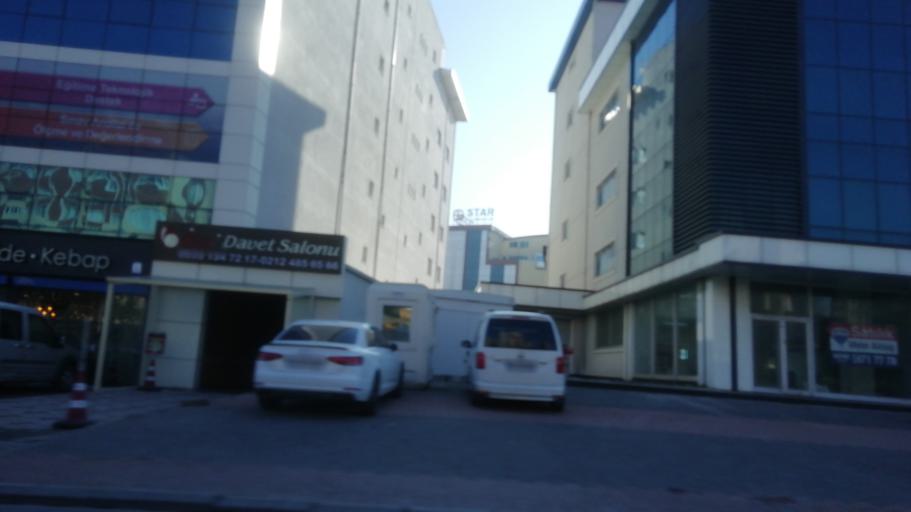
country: TR
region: Istanbul
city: Basaksehir
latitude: 41.1040
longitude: 28.7941
